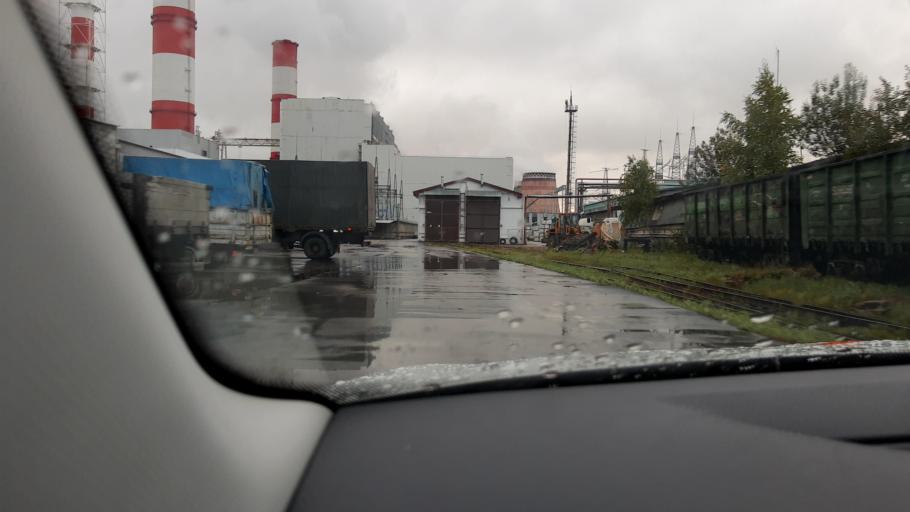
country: RU
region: Moscow
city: Annino
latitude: 55.5777
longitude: 37.6220
